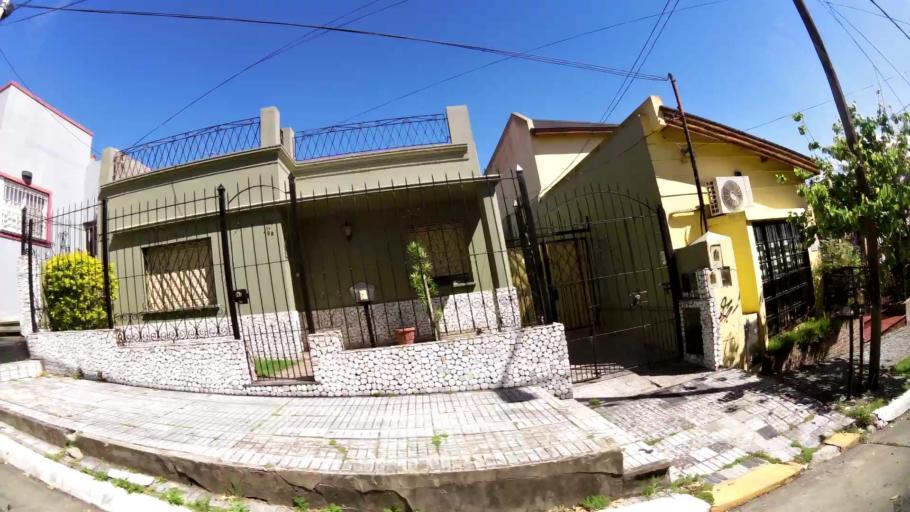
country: AR
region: Buenos Aires
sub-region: Partido de Quilmes
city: Quilmes
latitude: -34.7024
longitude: -58.2856
